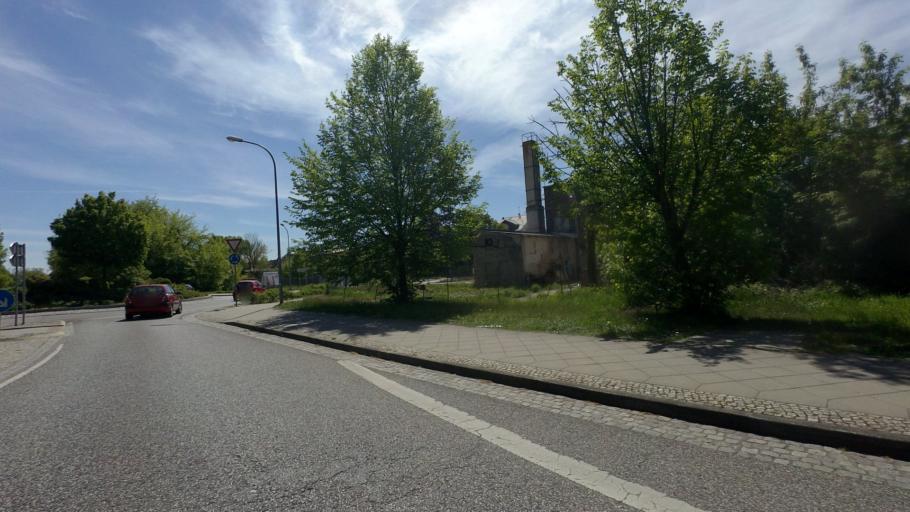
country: DE
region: Brandenburg
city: Luckenwalde
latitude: 52.0902
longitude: 13.1762
